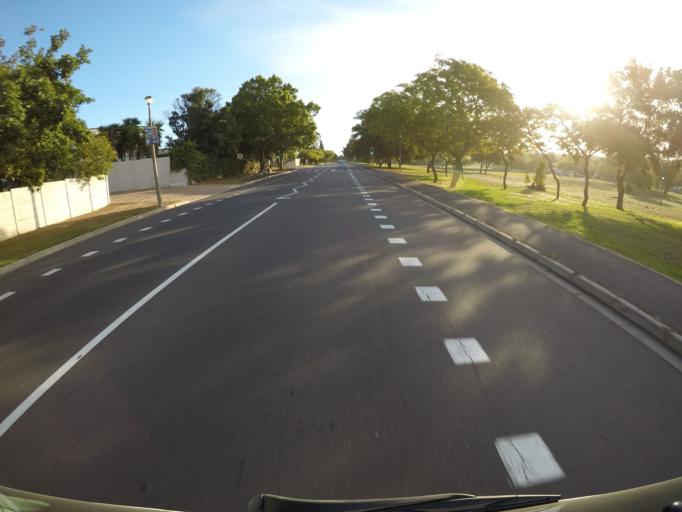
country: ZA
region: Western Cape
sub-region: City of Cape Town
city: Kraaifontein
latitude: -33.8656
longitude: 18.6553
